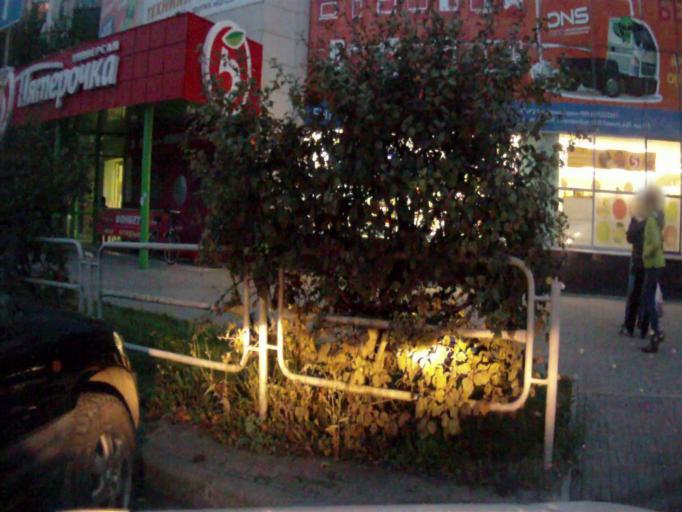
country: RU
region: Chelyabinsk
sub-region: Gorod Chelyabinsk
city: Chelyabinsk
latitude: 55.1871
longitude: 61.3321
